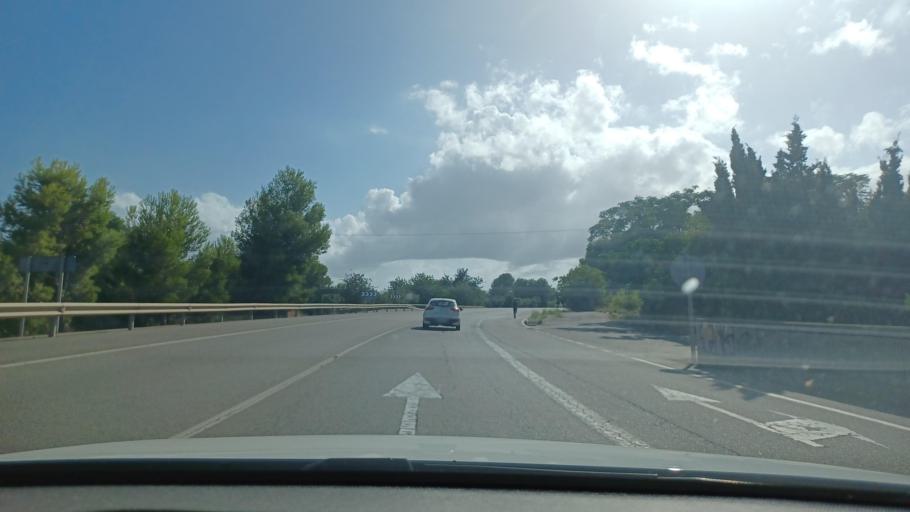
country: ES
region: Catalonia
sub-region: Provincia de Tarragona
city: Vilanova d'Escornalbou
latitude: 41.0279
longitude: 0.9626
